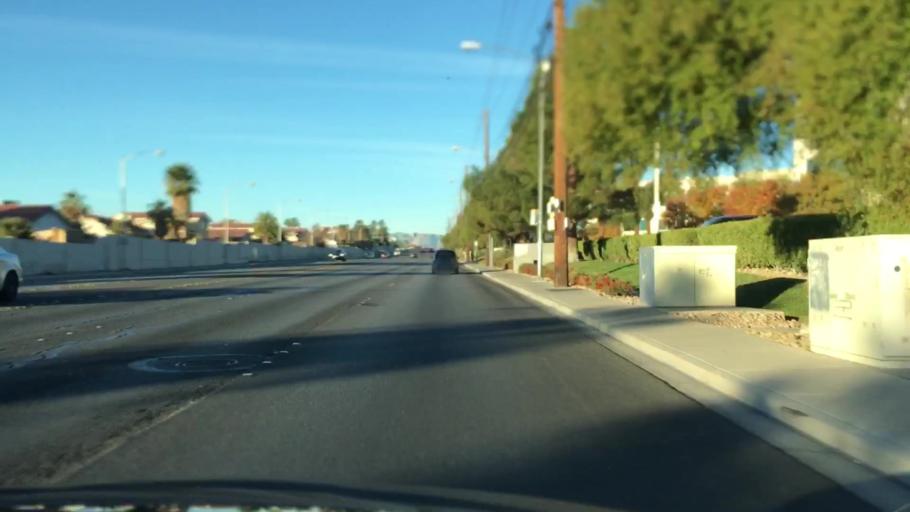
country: US
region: Nevada
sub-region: Clark County
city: Paradise
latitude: 36.0573
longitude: -115.1458
